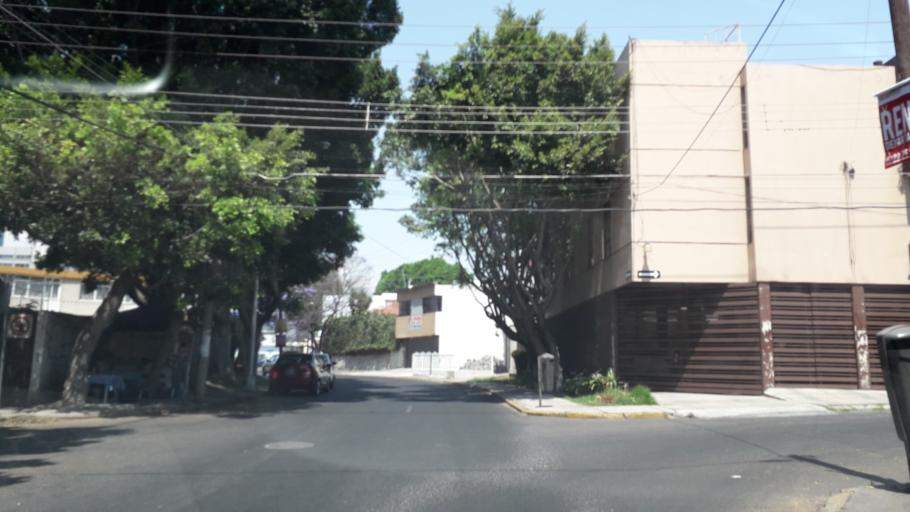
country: MX
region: Puebla
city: Puebla
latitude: 19.0536
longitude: -98.2186
